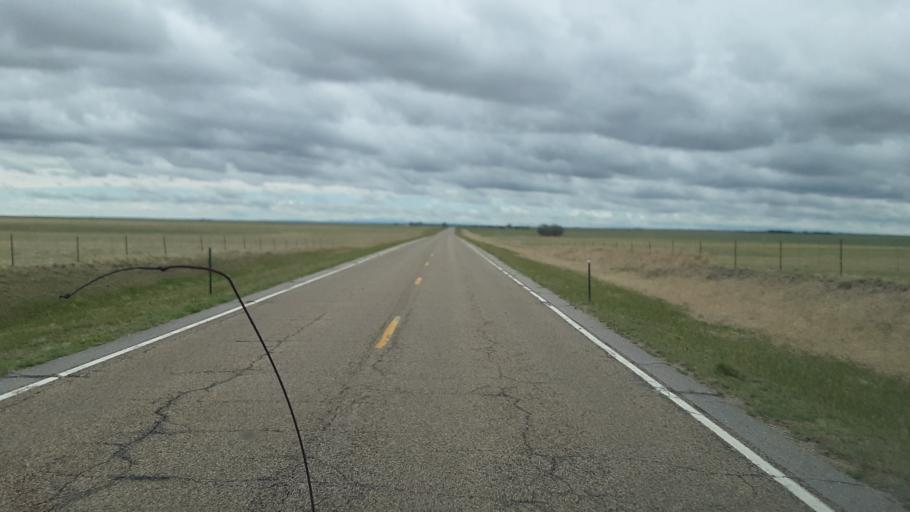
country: US
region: Colorado
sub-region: El Paso County
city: Ellicott
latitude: 38.8395
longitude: -103.9203
